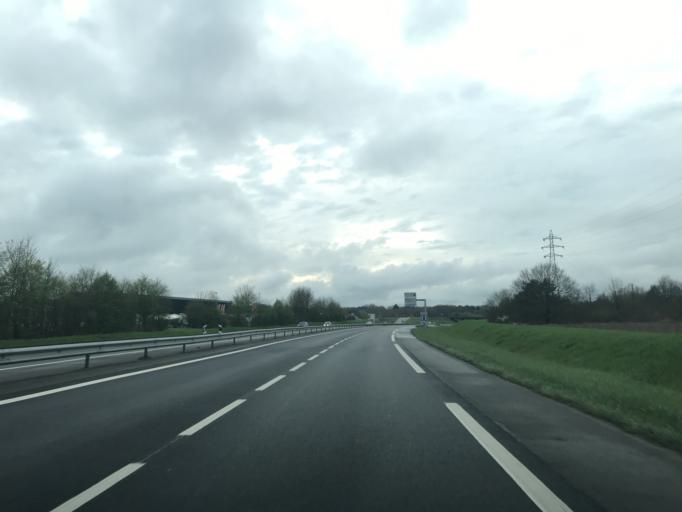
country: FR
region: Centre
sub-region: Departement du Loiret
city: Checy
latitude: 47.9068
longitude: 2.0412
